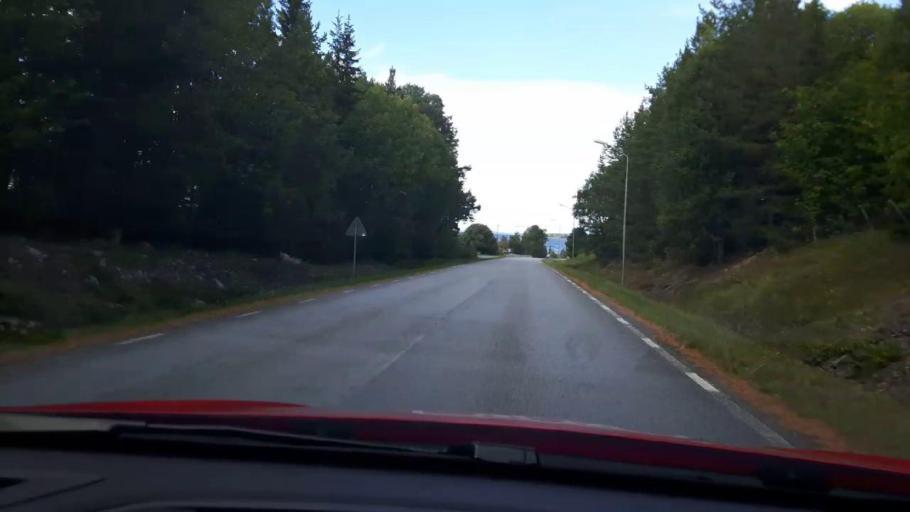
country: SE
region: Jaemtland
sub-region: Bergs Kommun
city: Hoverberg
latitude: 62.9788
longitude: 14.4819
